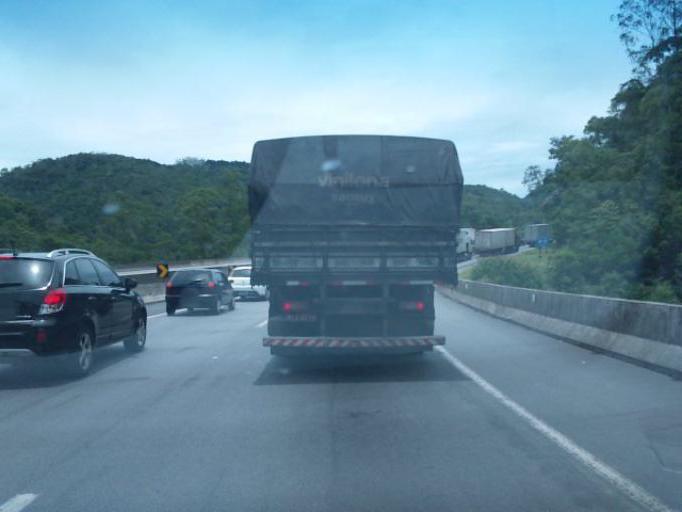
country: BR
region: Sao Paulo
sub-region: Juquitiba
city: Juquitiba
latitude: -24.0515
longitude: -47.2018
